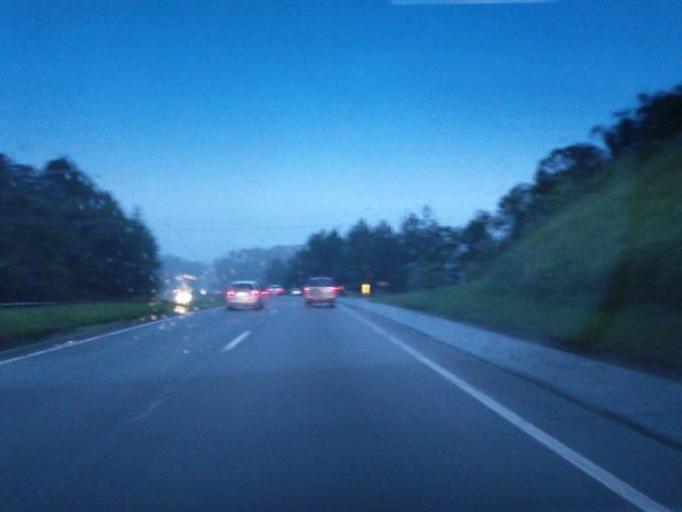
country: BR
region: Sao Paulo
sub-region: Juquitiba
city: Juquitiba
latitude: -23.9640
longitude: -47.1246
